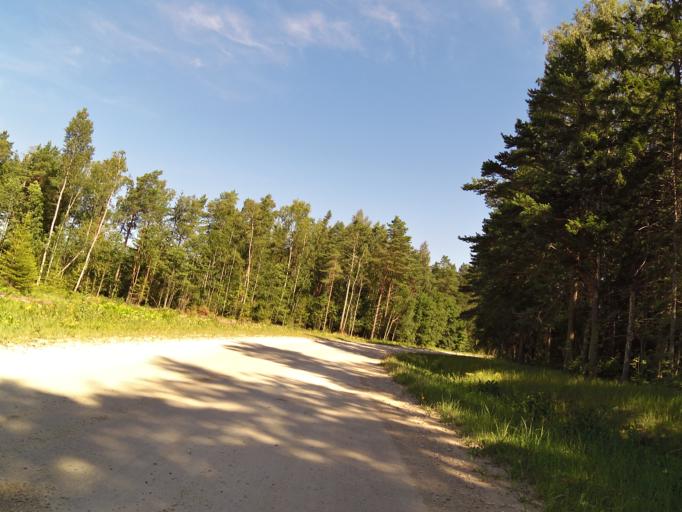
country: EE
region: Hiiumaa
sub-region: Kaerdla linn
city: Kardla
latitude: 58.9295
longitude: 22.3727
